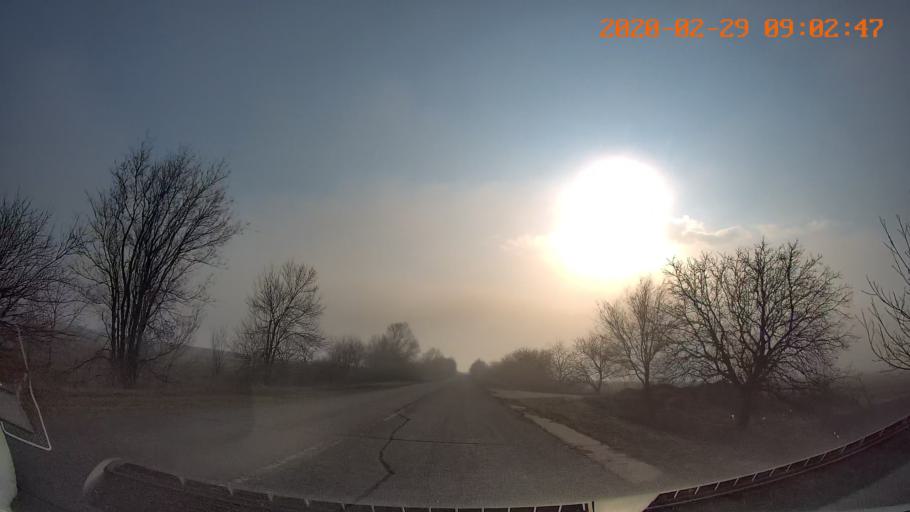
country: UA
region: Odessa
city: Velykoploske
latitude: 46.9192
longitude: 29.7169
